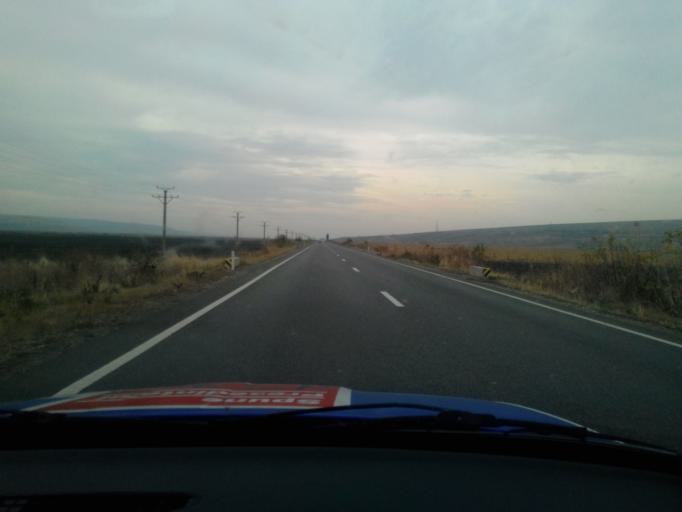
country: RO
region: Vaslui
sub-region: Comuna Banca
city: Banca
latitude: 46.3210
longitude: 27.7529
